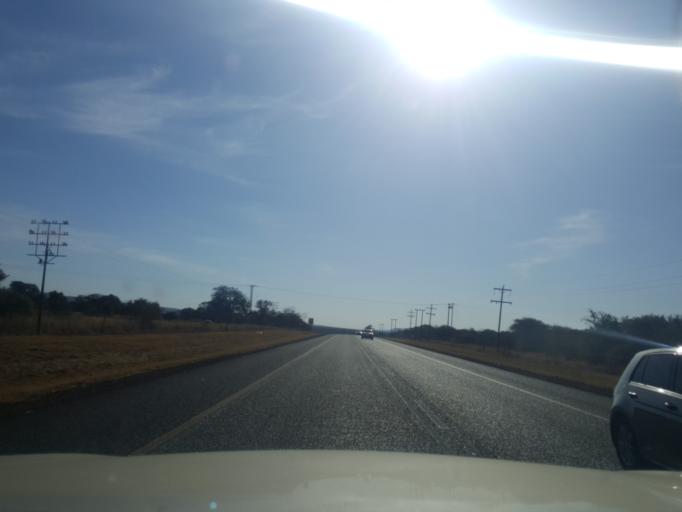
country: ZA
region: North-West
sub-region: Ngaka Modiri Molema District Municipality
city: Zeerust
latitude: -25.5223
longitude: 26.1792
